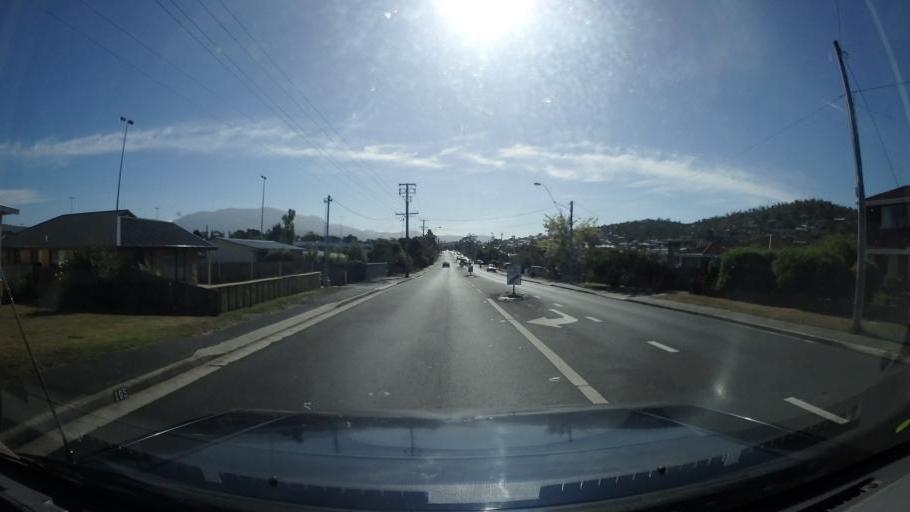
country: AU
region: Tasmania
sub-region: Clarence
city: Howrah
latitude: -42.8777
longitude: 147.3948
